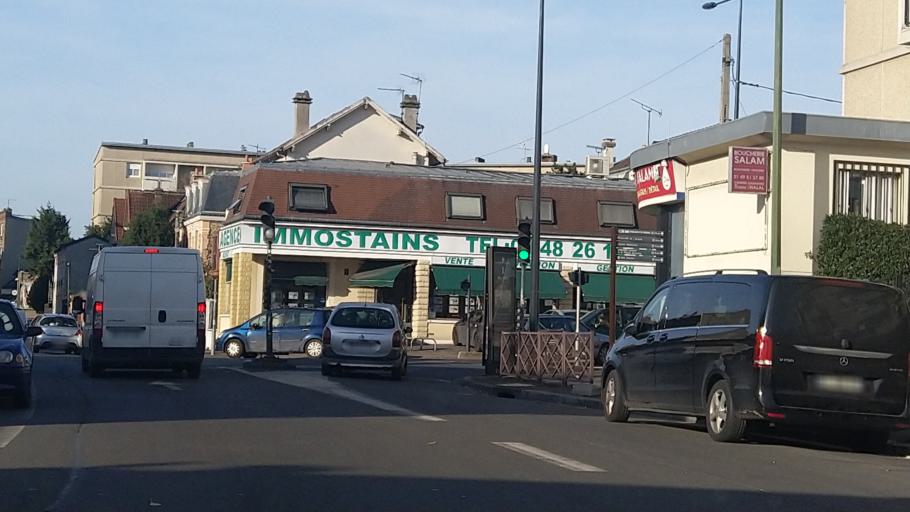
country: FR
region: Ile-de-France
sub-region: Departement de Seine-Saint-Denis
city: Stains
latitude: 48.9607
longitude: 2.3818
